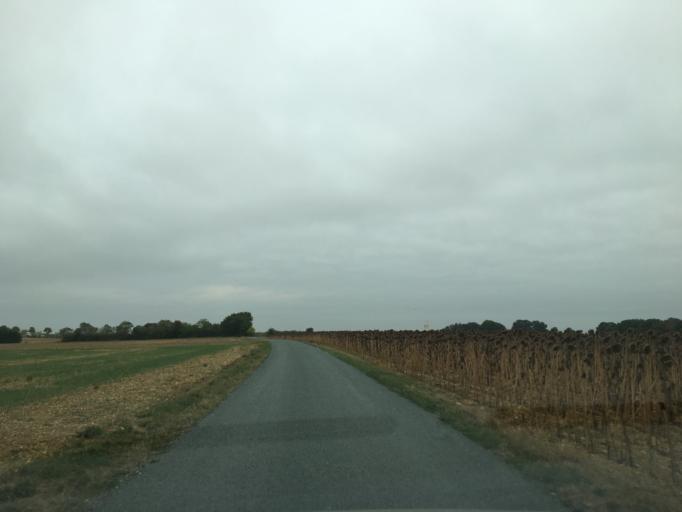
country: FR
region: Poitou-Charentes
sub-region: Departement des Deux-Sevres
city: Beauvoir-sur-Niort
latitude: 46.0857
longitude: -0.4958
